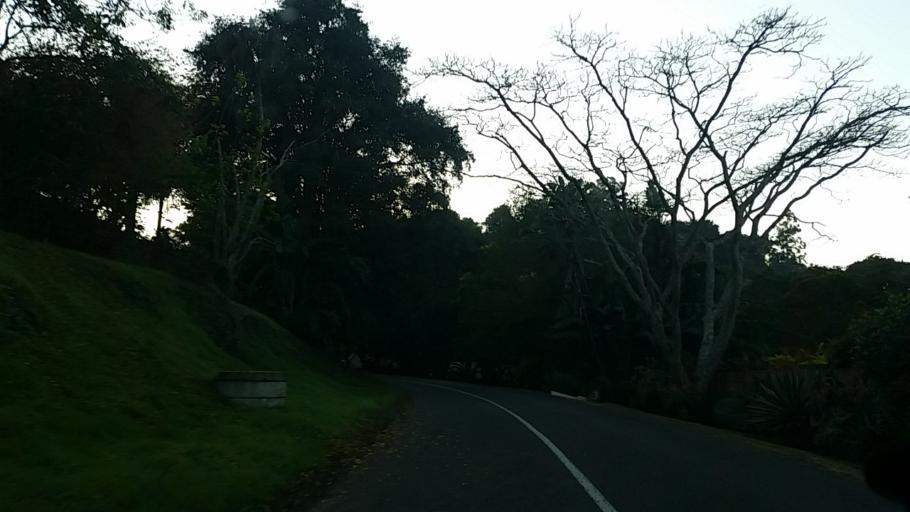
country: ZA
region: KwaZulu-Natal
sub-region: eThekwini Metropolitan Municipality
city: Berea
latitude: -29.8465
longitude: 30.9067
